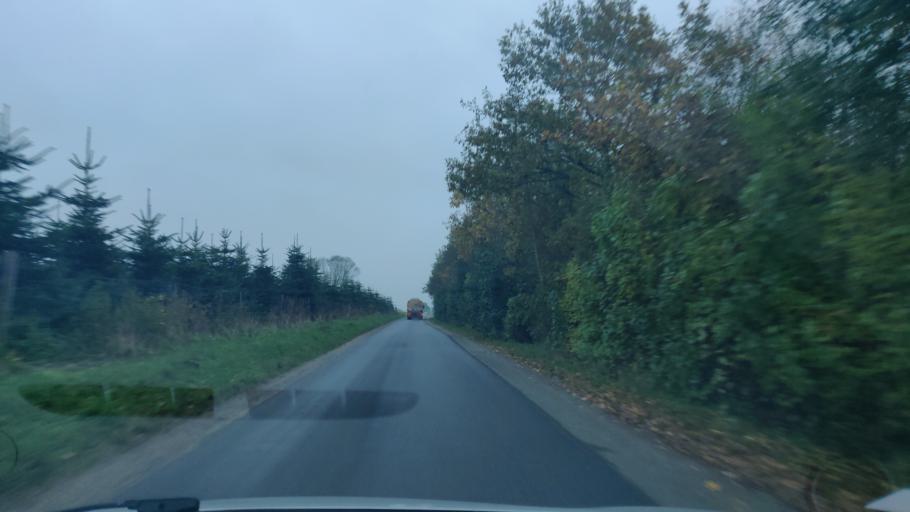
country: DK
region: South Denmark
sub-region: Kolding Kommune
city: Kolding
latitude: 55.5742
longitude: 9.4477
